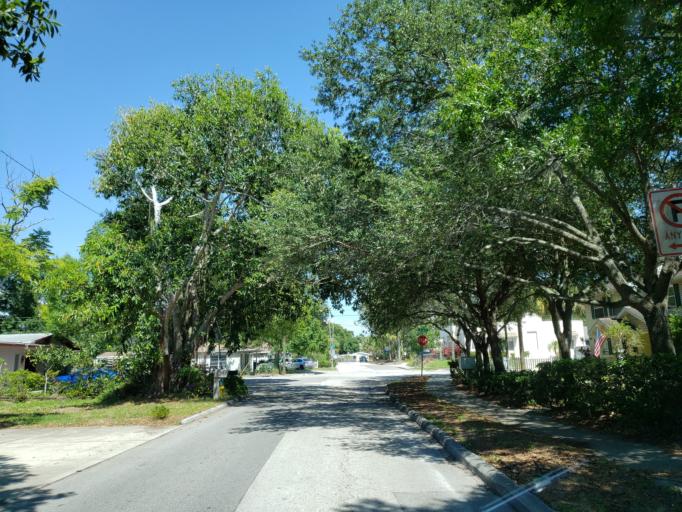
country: US
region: Florida
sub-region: Hillsborough County
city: Tampa
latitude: 27.9467
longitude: -82.5145
